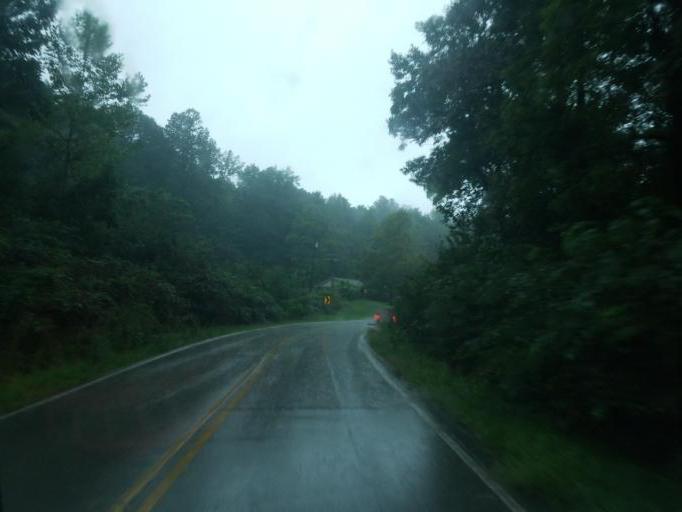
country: US
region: Kentucky
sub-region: Carter County
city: Olive Hill
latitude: 38.3419
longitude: -83.2012
